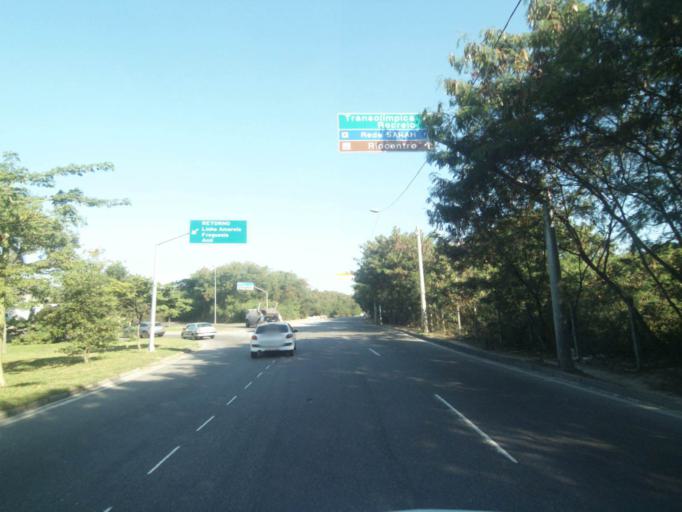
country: BR
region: Rio de Janeiro
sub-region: Sao Joao De Meriti
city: Sao Joao de Meriti
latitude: -22.9559
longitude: -43.3584
